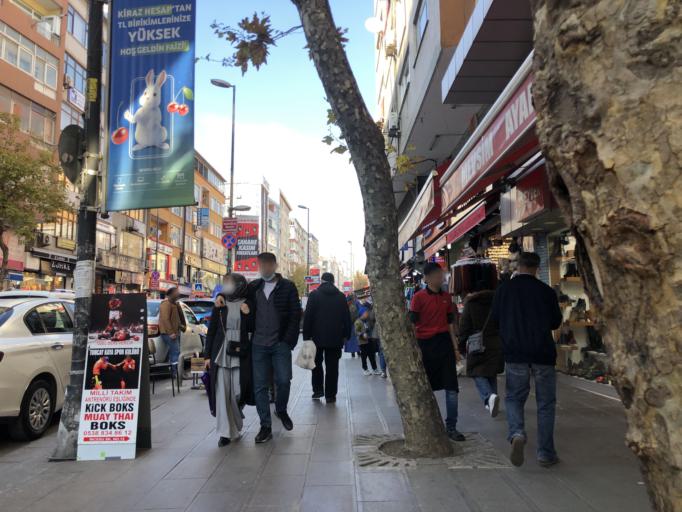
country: TR
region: Istanbul
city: Bahcelievler
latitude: 40.9933
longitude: 28.8433
